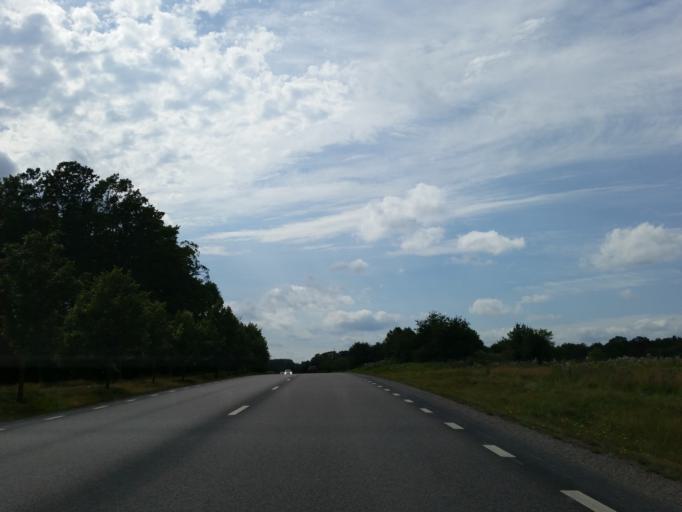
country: SE
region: Soedermanland
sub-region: Strangnas Kommun
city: Mariefred
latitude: 59.2577
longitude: 17.1941
